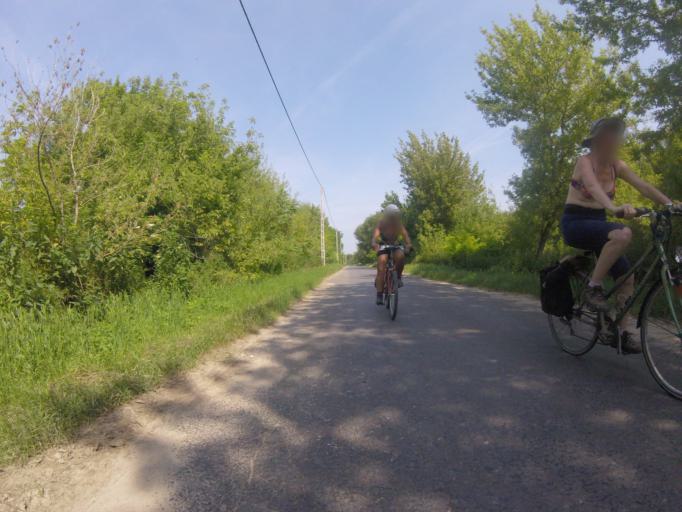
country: HU
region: Tolna
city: Bolcske
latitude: 46.7311
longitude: 18.9250
